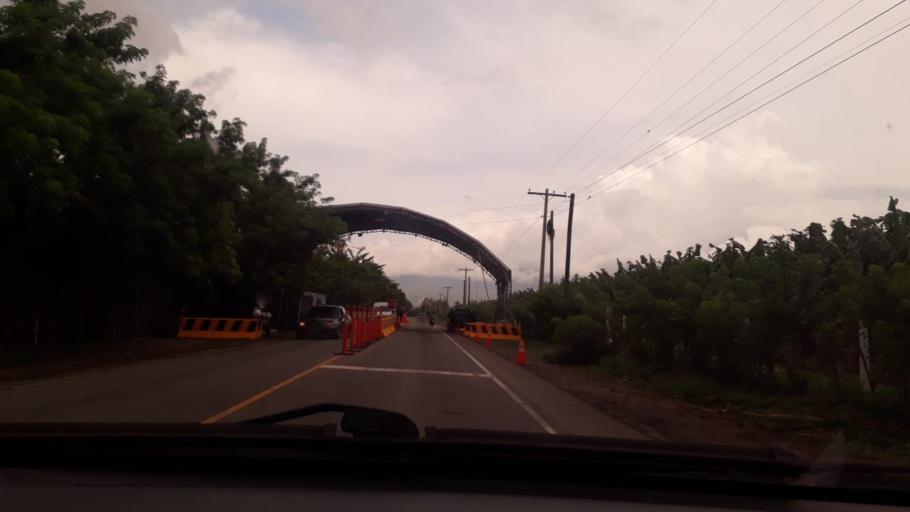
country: HN
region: Cortes
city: Potrerillos
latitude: 15.6383
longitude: -88.4158
